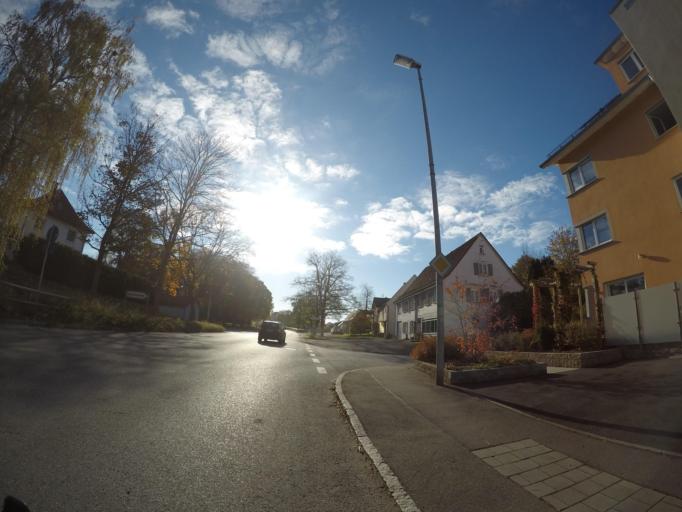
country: DE
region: Baden-Wuerttemberg
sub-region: Tuebingen Region
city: Herbertingen
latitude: 48.0591
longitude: 9.4403
